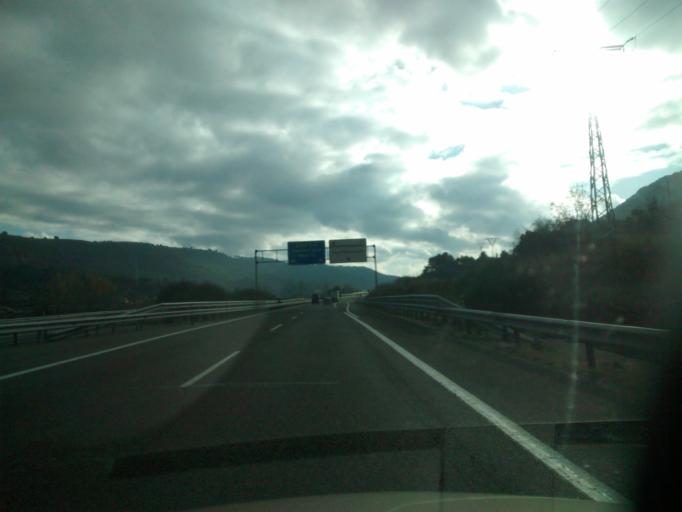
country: ES
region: Castille-La Mancha
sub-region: Provincia de Guadalajara
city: Tortola de Henares
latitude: 40.6916
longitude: -3.0865
